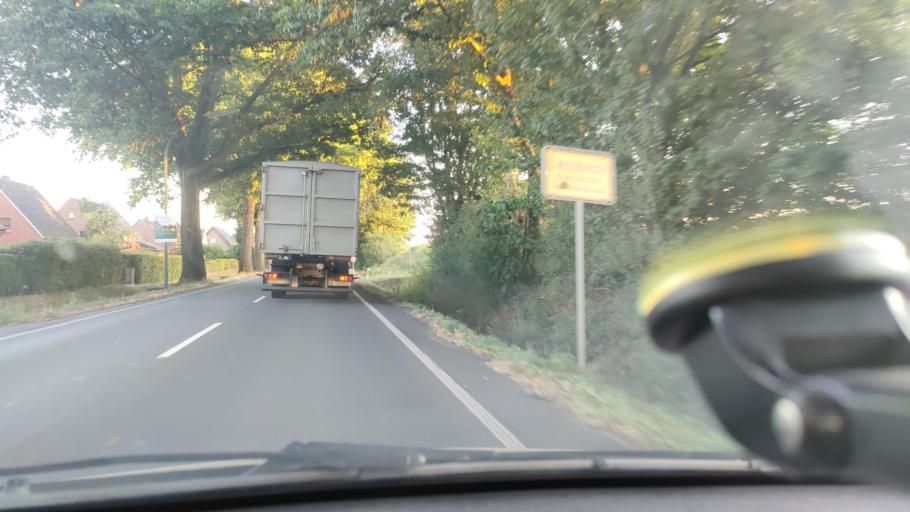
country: DE
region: North Rhine-Westphalia
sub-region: Regierungsbezirk Munster
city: Klein Reken
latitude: 51.7658
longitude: 6.9990
